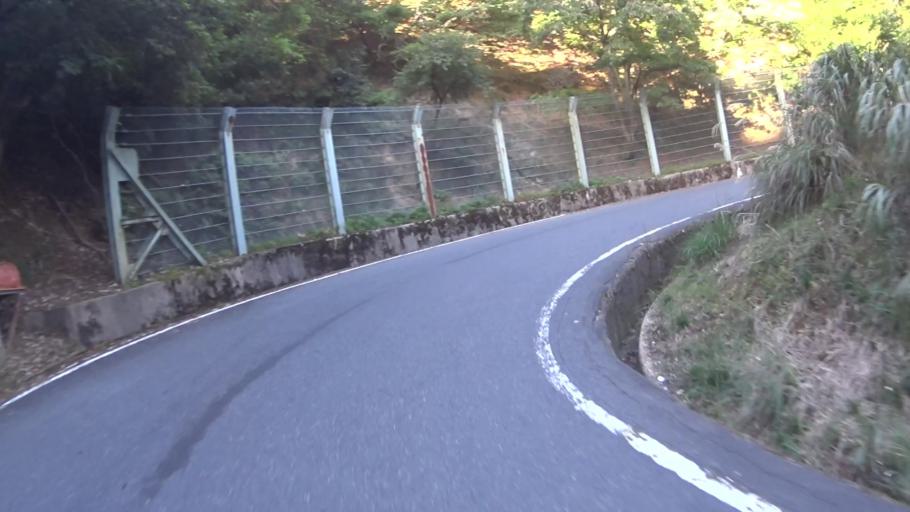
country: JP
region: Hyogo
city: Toyooka
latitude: 35.6152
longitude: 134.8728
